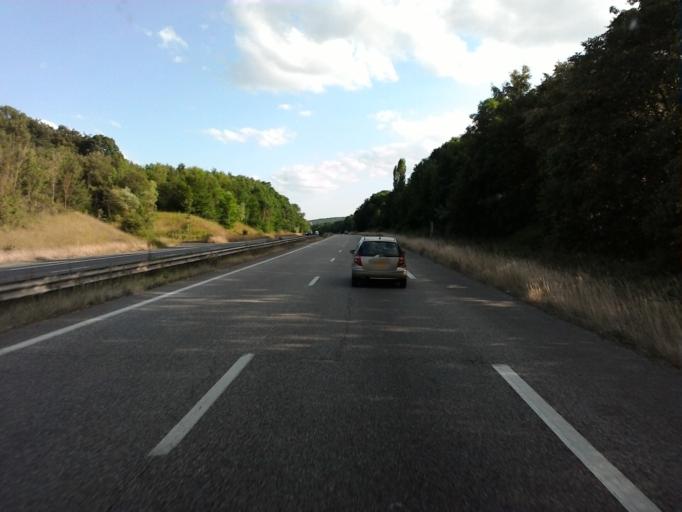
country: FR
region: Lorraine
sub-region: Departement de Meurthe-et-Moselle
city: Richardmenil
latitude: 48.6022
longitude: 6.1725
